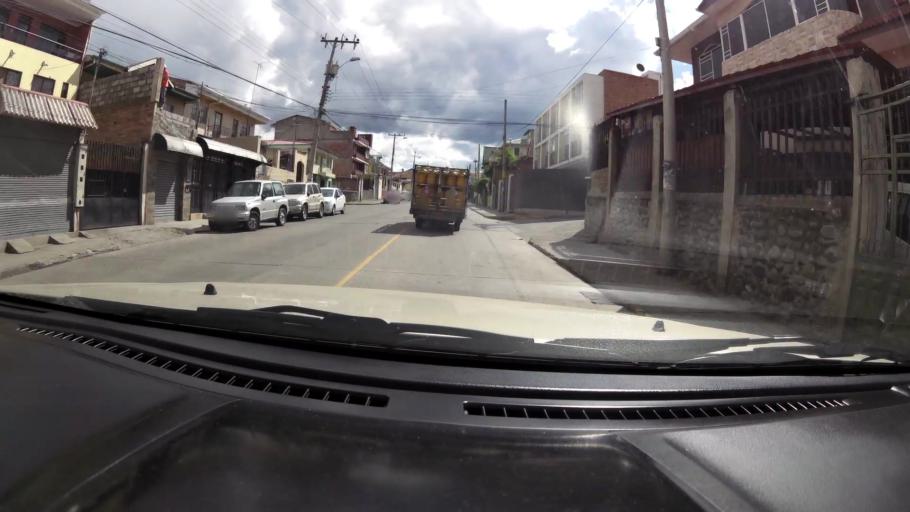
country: EC
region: Azuay
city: Cuenca
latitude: -2.8868
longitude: -78.9928
